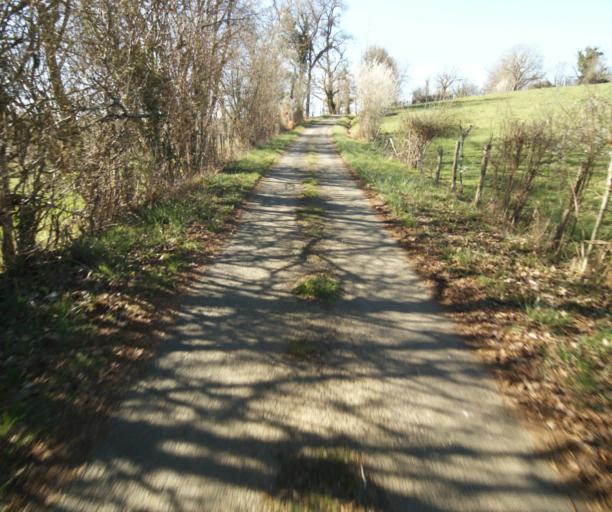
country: FR
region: Limousin
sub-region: Departement de la Correze
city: Chamboulive
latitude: 45.4030
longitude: 1.7042
